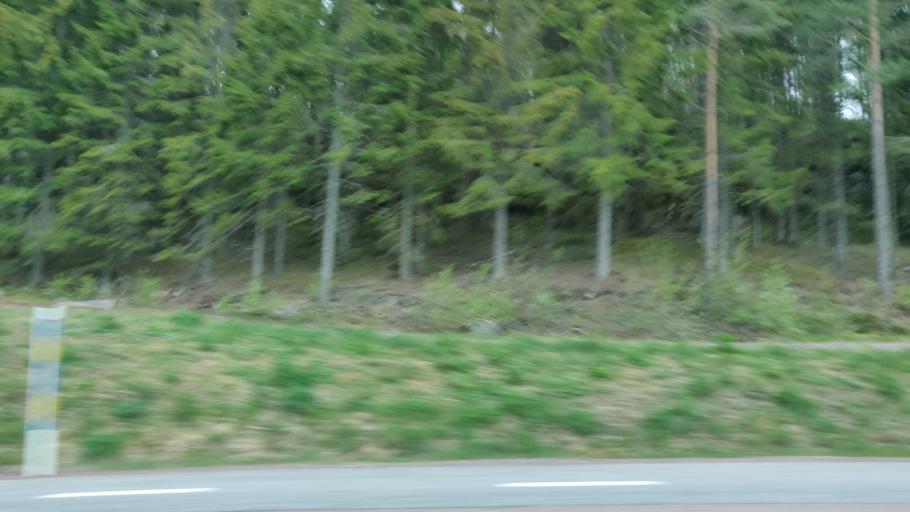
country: SE
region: Vaermland
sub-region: Forshaga Kommun
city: Deje
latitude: 59.6856
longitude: 13.4394
